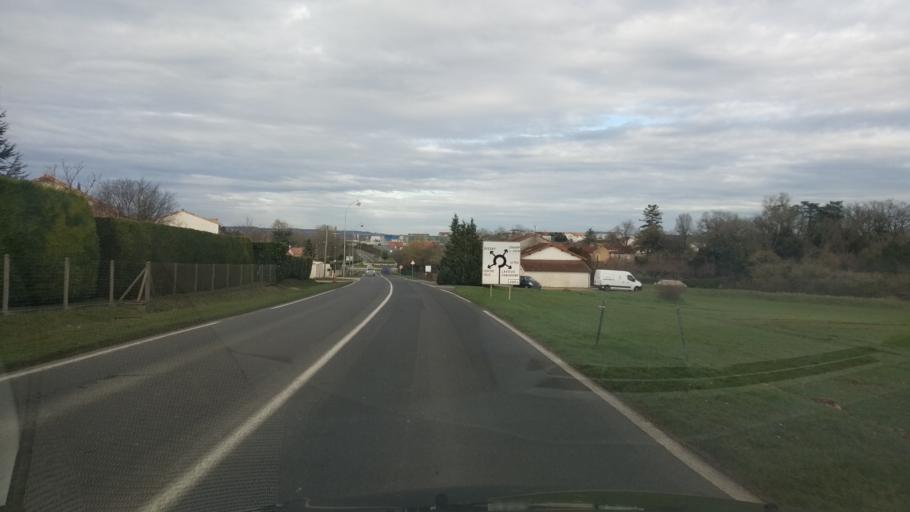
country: FR
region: Poitou-Charentes
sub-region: Departement de la Vienne
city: Saint-Georges-les-Baillargeaux
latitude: 46.6654
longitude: 0.4014
